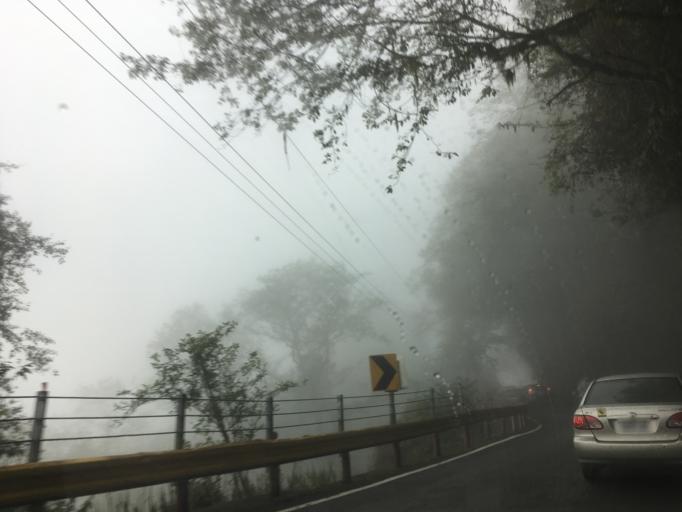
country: TW
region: Taiwan
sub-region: Hualien
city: Hualian
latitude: 24.1882
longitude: 121.4106
